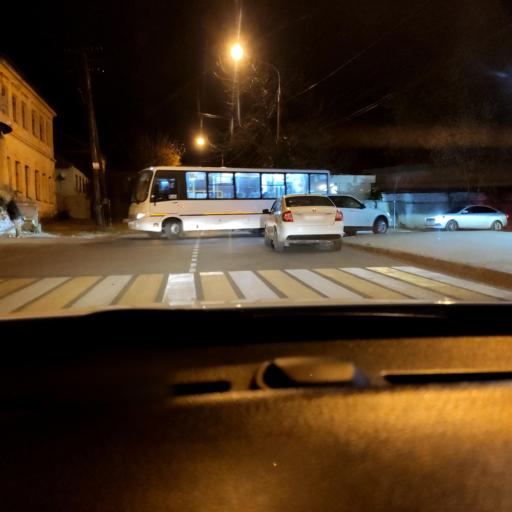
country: RU
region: Voronezj
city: Voronezh
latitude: 51.6816
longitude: 39.2208
